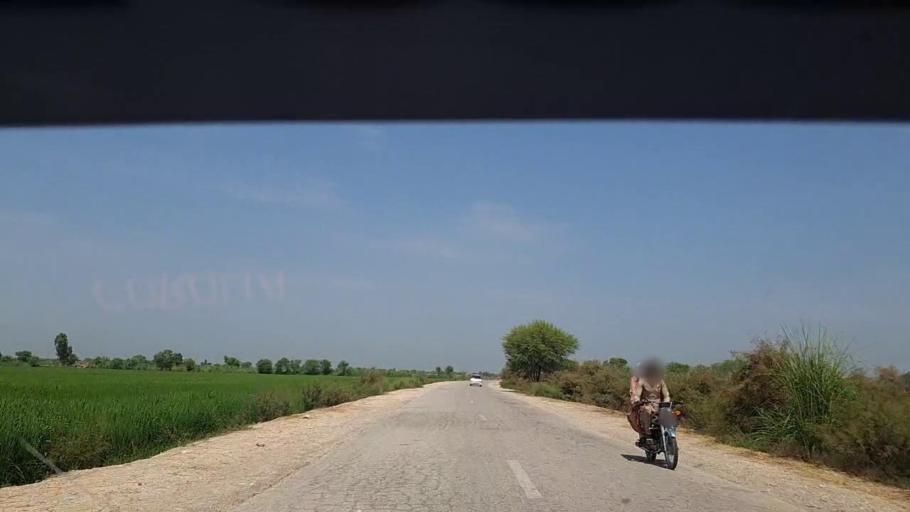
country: PK
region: Sindh
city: Thul
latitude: 28.1334
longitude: 68.8177
